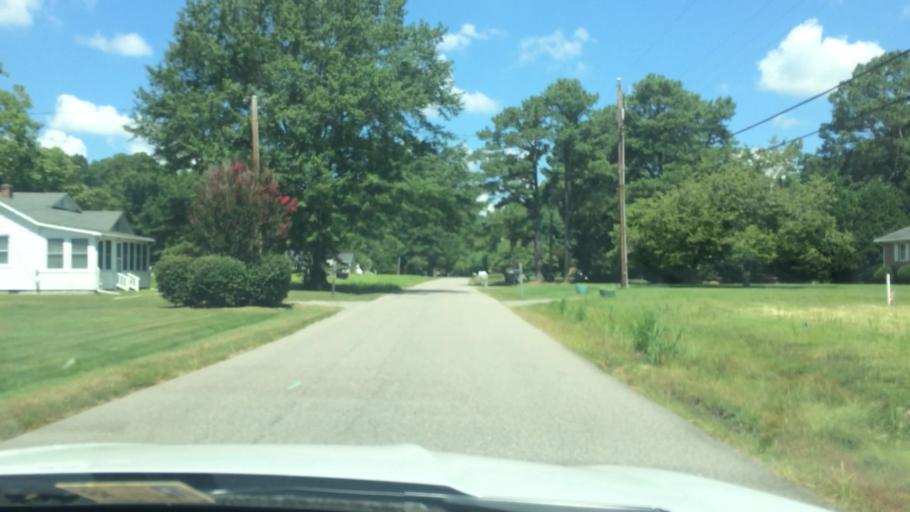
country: US
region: Virginia
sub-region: King William County
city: West Point
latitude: 37.5664
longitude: -76.8025
